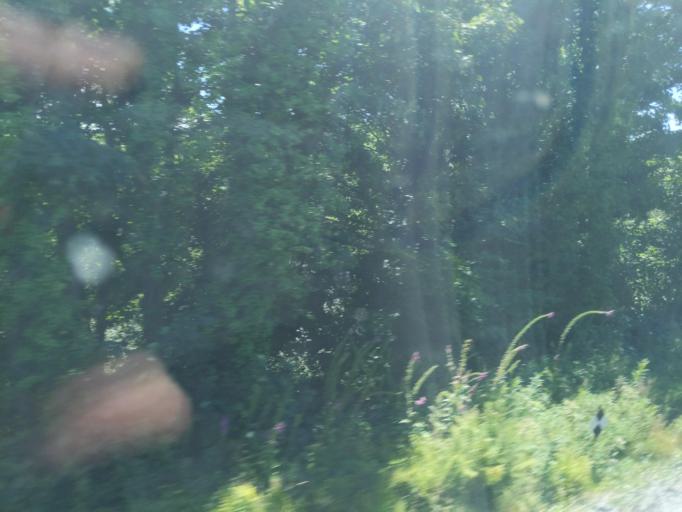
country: GB
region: England
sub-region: Cornwall
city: St Austell
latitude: 50.3397
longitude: -4.8257
